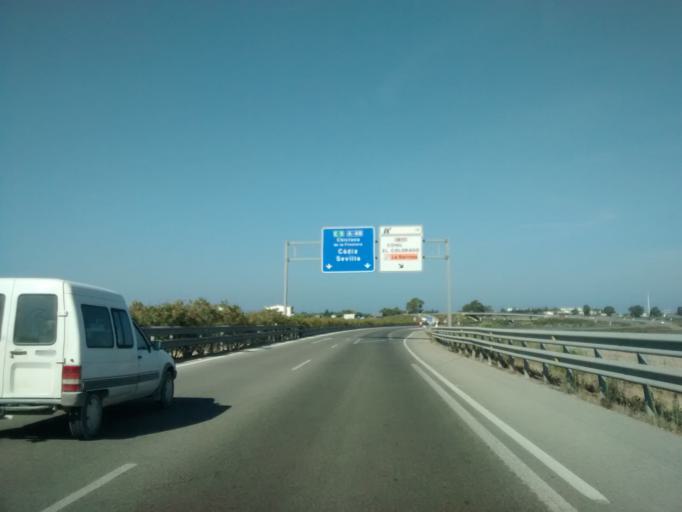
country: ES
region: Andalusia
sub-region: Provincia de Cadiz
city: Conil de la Frontera
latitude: 36.3555
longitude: -6.0978
